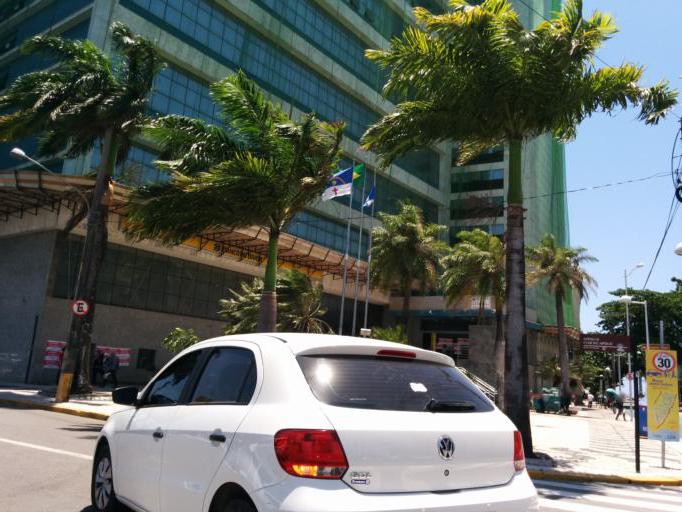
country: BR
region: Pernambuco
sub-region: Recife
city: Recife
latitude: -8.0623
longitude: -34.8738
